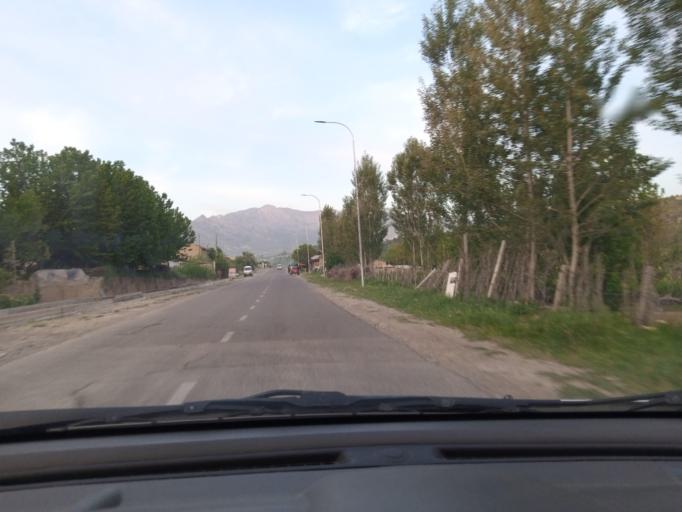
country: UZ
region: Toshkent
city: Parkent
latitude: 41.2451
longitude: 69.7434
